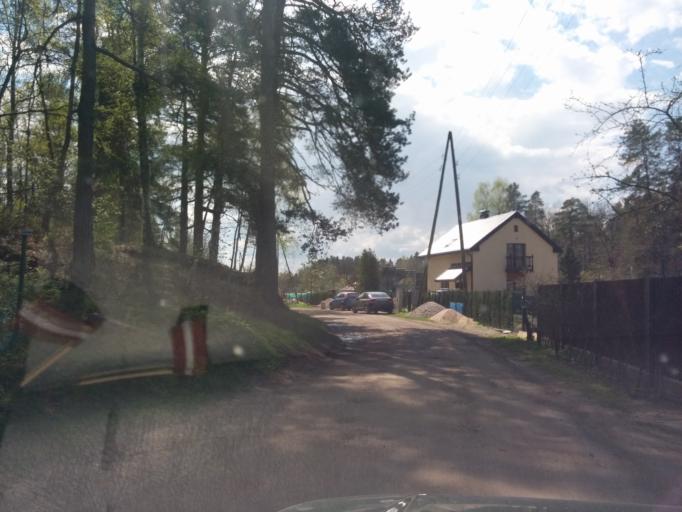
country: LV
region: Ozolnieku
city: Ozolnieki
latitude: 56.6281
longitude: 23.7754
